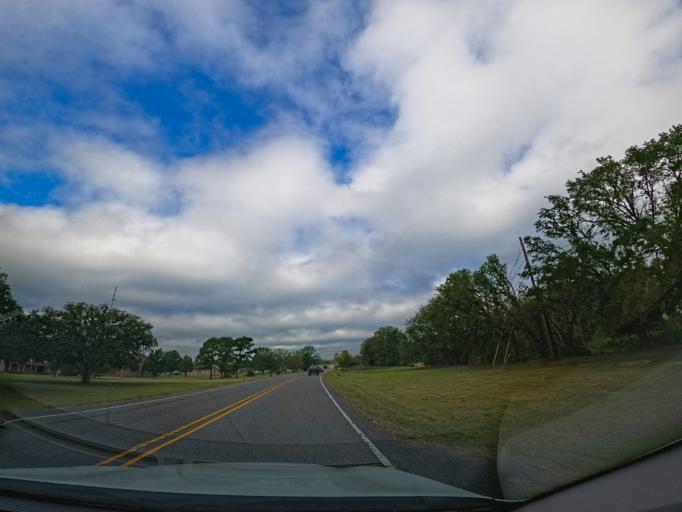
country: US
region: Louisiana
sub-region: Terrebonne Parish
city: Gray
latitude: 29.6091
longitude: -90.8910
